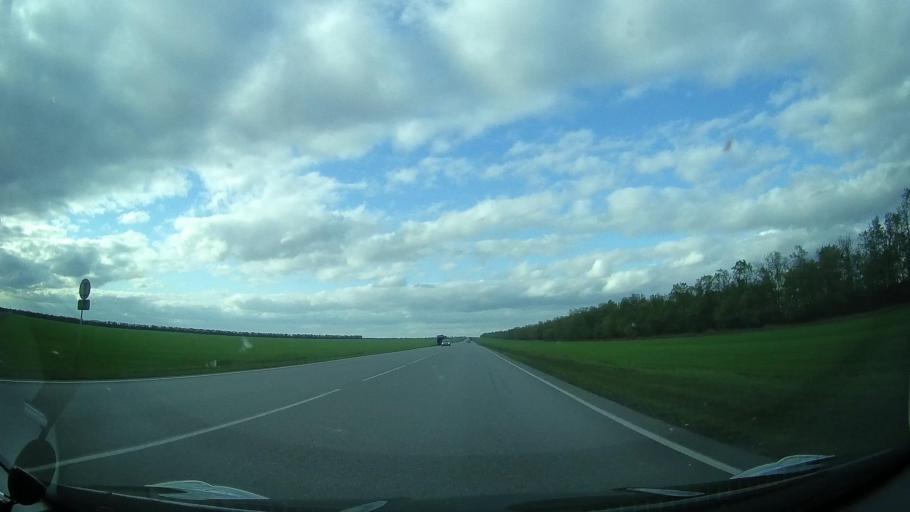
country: RU
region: Rostov
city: Kagal'nitskaya
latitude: 46.9039
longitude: 40.1202
